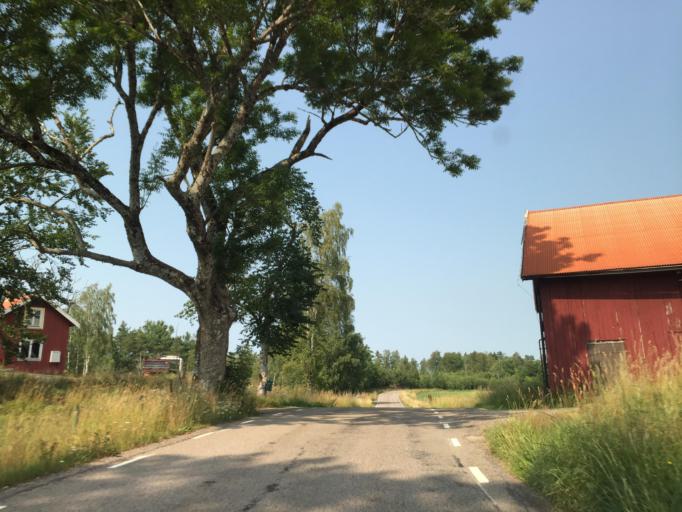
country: SE
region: Vaestra Goetaland
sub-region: Trollhattan
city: Sjuntorp
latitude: 58.3279
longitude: 12.1233
